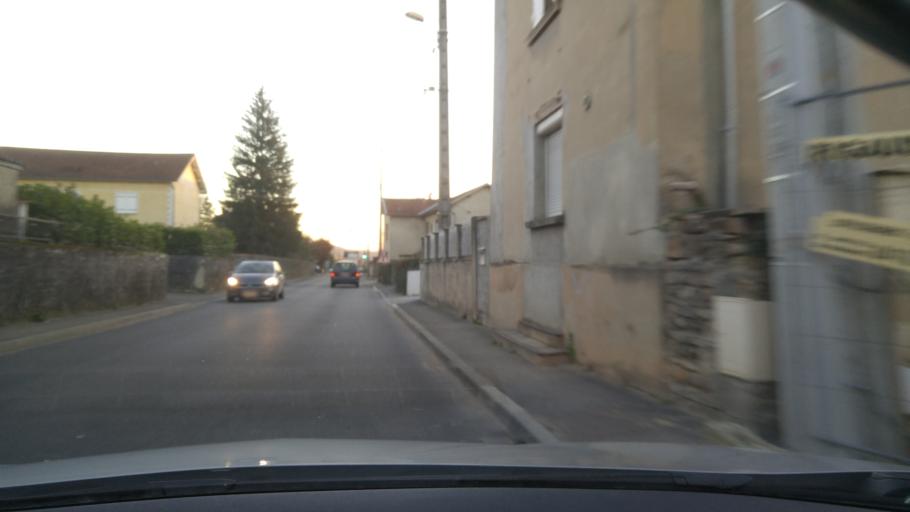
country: FR
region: Rhone-Alpes
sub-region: Departement de l'Isere
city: Tignieu-Jameyzieu
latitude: 45.7348
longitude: 5.1875
